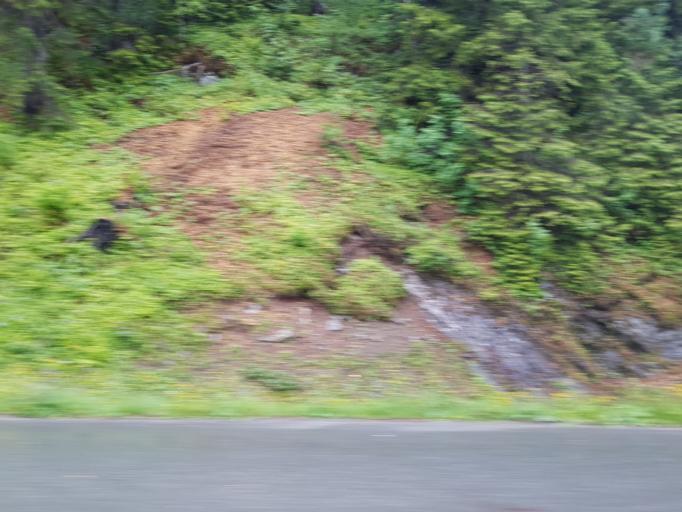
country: NO
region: Sor-Trondelag
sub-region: Selbu
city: Mebonden
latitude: 63.3320
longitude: 11.0910
